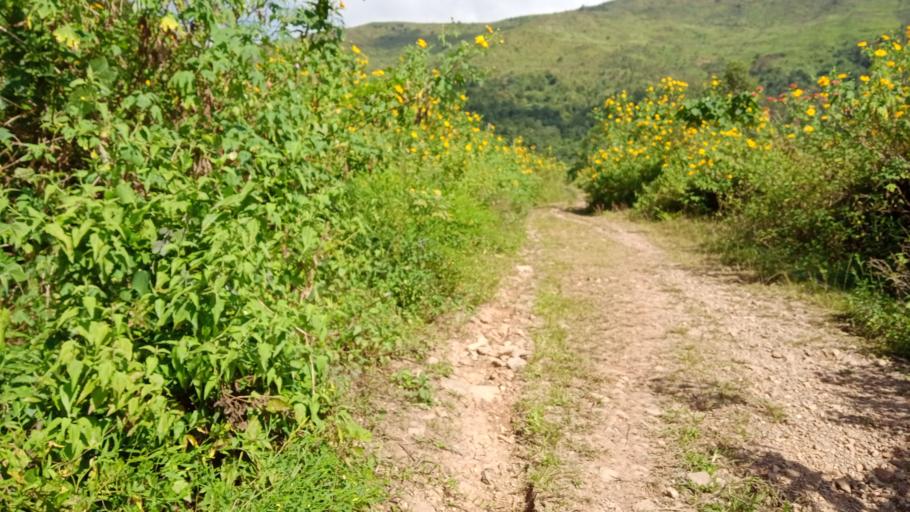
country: LA
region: Xiangkhoang
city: Phonsavan
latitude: 19.1133
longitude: 102.9249
